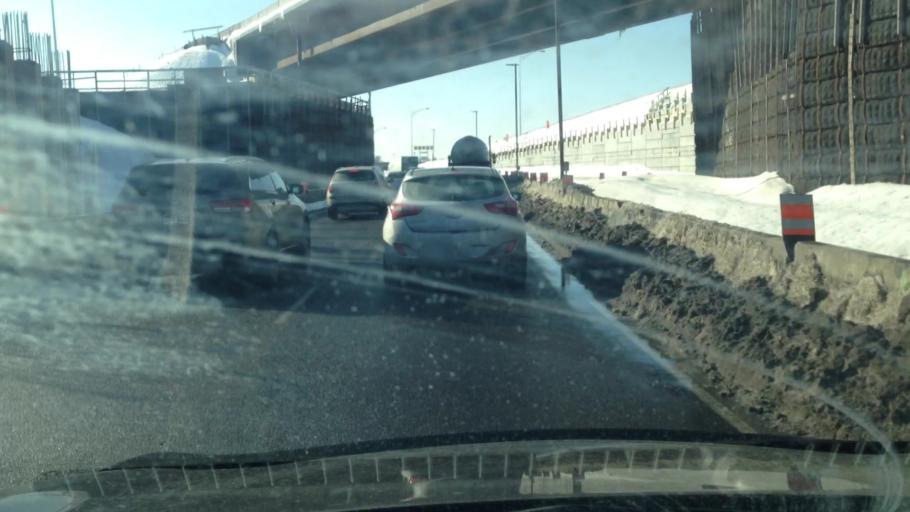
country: CA
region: Quebec
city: Montreal-Ouest
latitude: 45.4509
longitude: -73.6326
